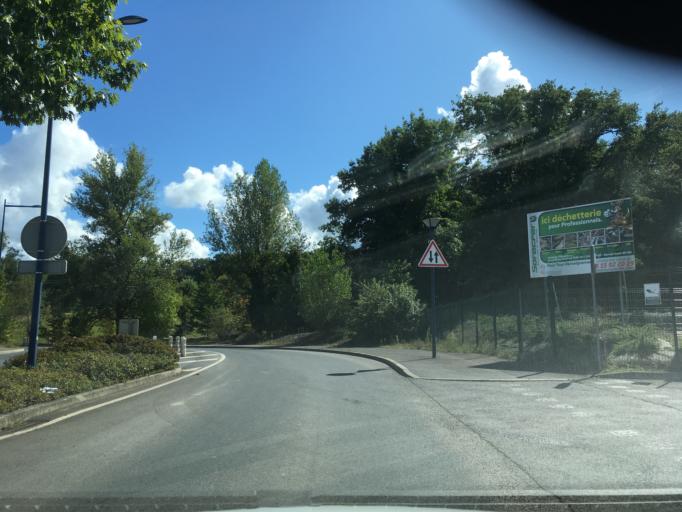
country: FR
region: Limousin
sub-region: Departement de la Correze
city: Saint-Pantaleon-de-Larche
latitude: 45.1382
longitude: 1.4779
